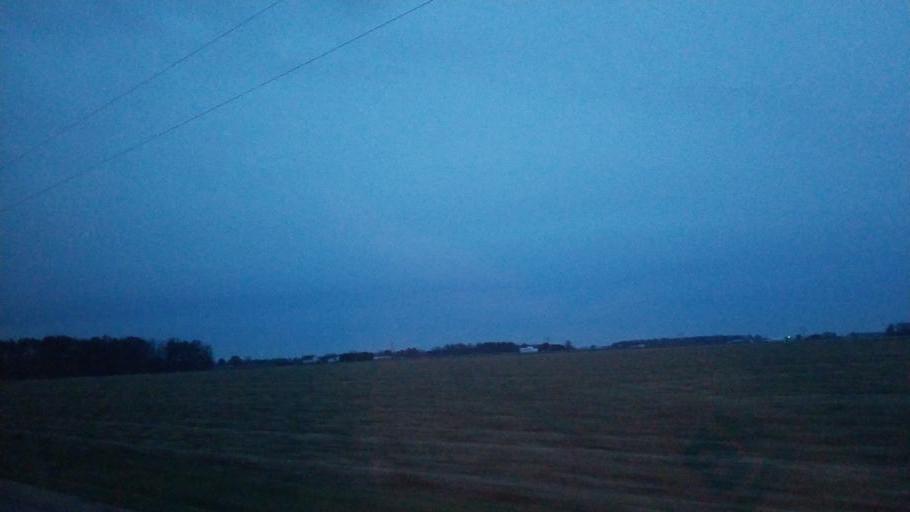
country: US
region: Indiana
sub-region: Adams County
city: Berne
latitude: 40.7020
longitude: -84.9940
